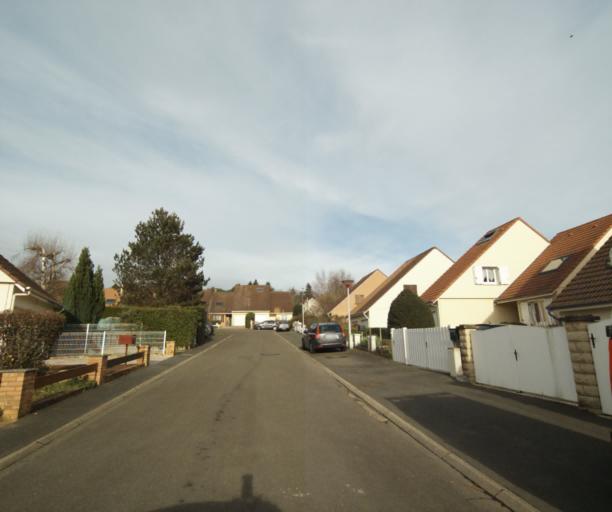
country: FR
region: Pays de la Loire
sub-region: Departement de la Sarthe
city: Sarge-les-le-Mans
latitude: 48.0026
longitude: 0.2348
